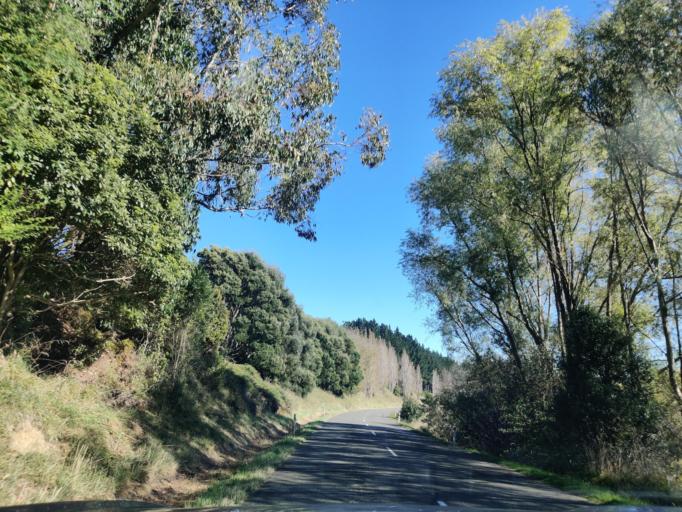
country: NZ
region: Manawatu-Wanganui
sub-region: Palmerston North City
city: Palmerston North
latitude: -40.2583
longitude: 175.7075
